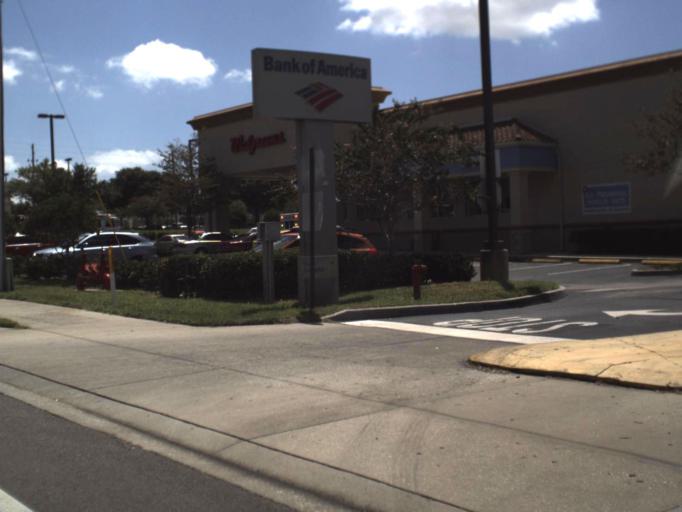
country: US
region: Florida
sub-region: Pinellas County
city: Dunedin
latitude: 28.0194
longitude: -82.7645
